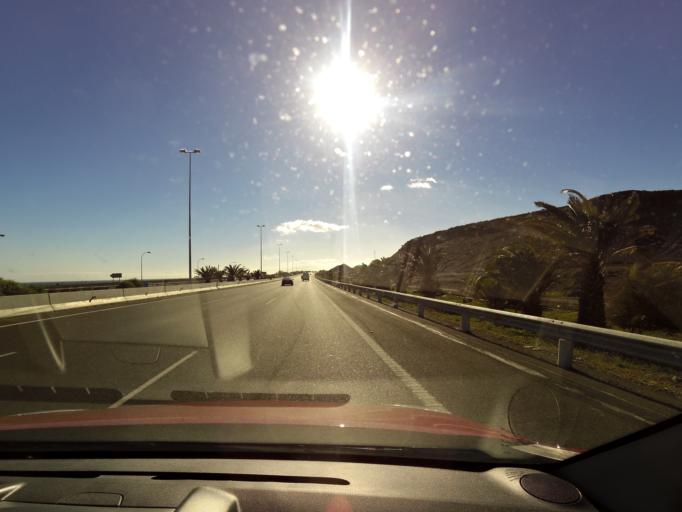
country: ES
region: Canary Islands
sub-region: Provincia de Las Palmas
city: Cruce de Arinaga
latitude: 27.8041
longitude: -15.4834
